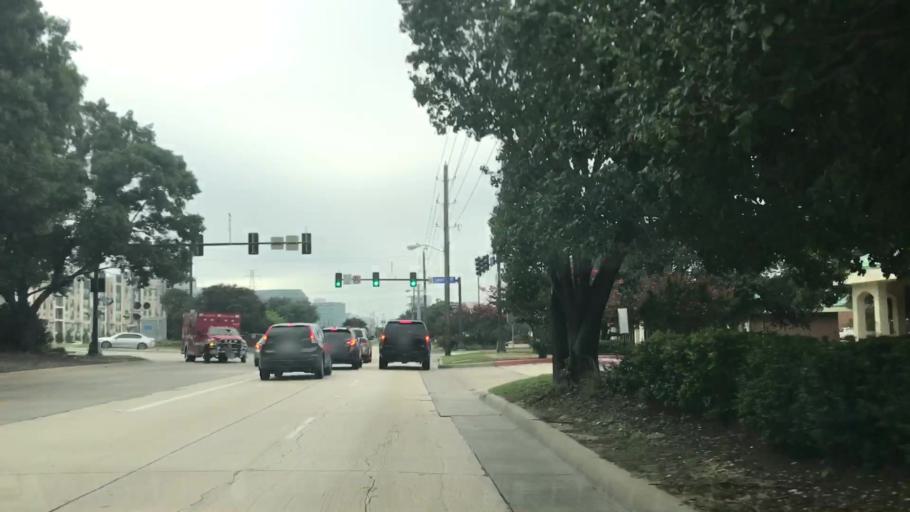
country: US
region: Texas
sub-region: Dallas County
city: Addison
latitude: 32.9483
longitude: -96.8287
